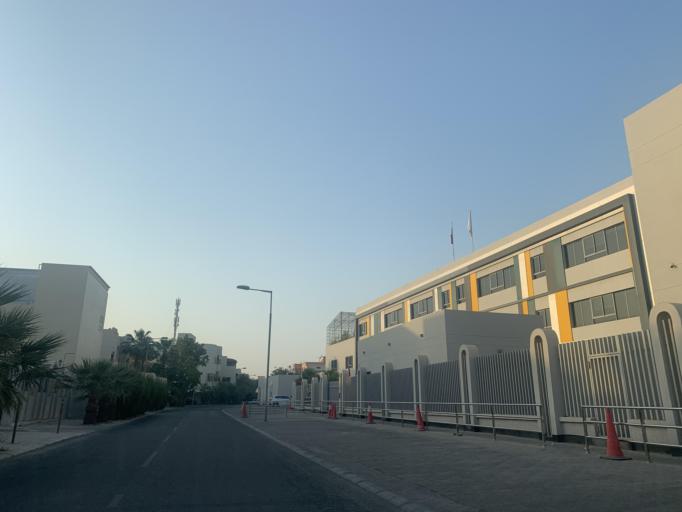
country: BH
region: Manama
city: Jidd Hafs
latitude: 26.2138
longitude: 50.5279
